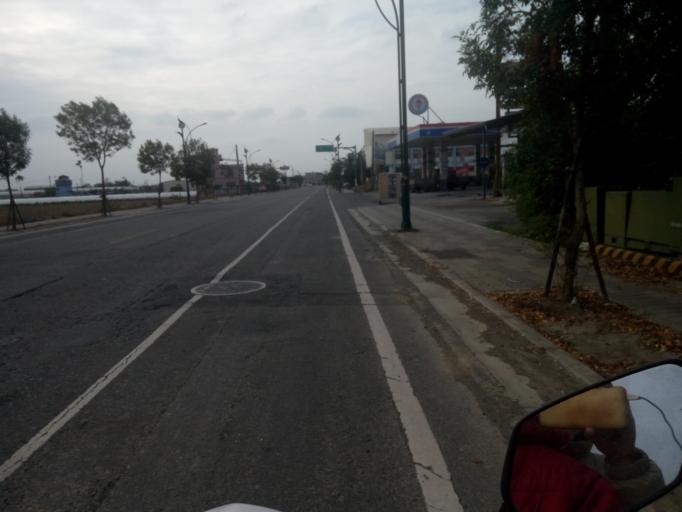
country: TW
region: Taiwan
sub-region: Chiayi
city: Taibao
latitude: 23.4923
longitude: 120.3413
